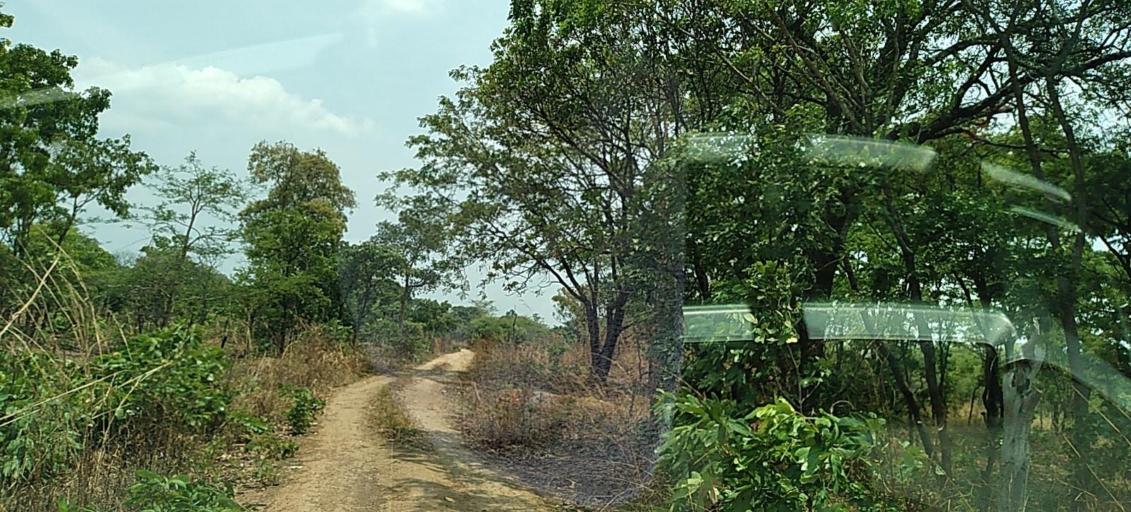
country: ZM
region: Copperbelt
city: Chililabombwe
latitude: -12.3763
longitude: 27.6428
